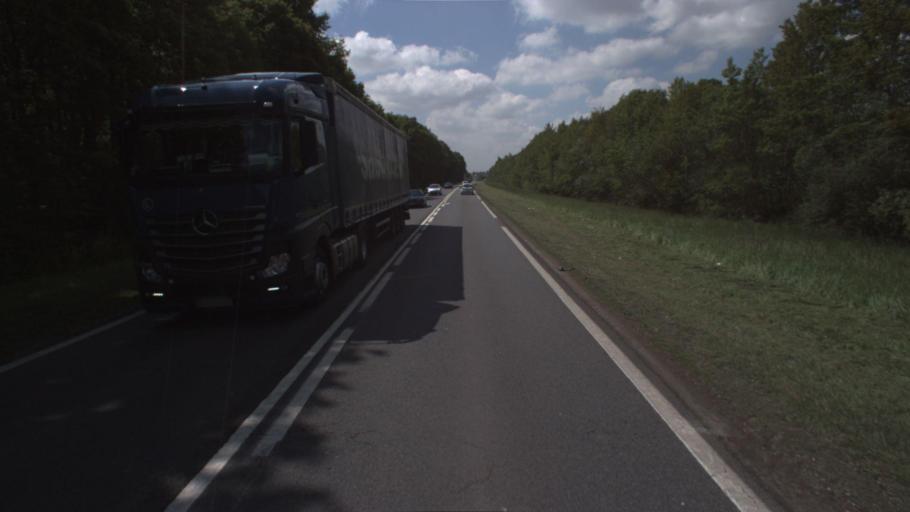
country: FR
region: Ile-de-France
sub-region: Departement de Seine-et-Marne
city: Guignes
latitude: 48.6488
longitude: 2.8017
